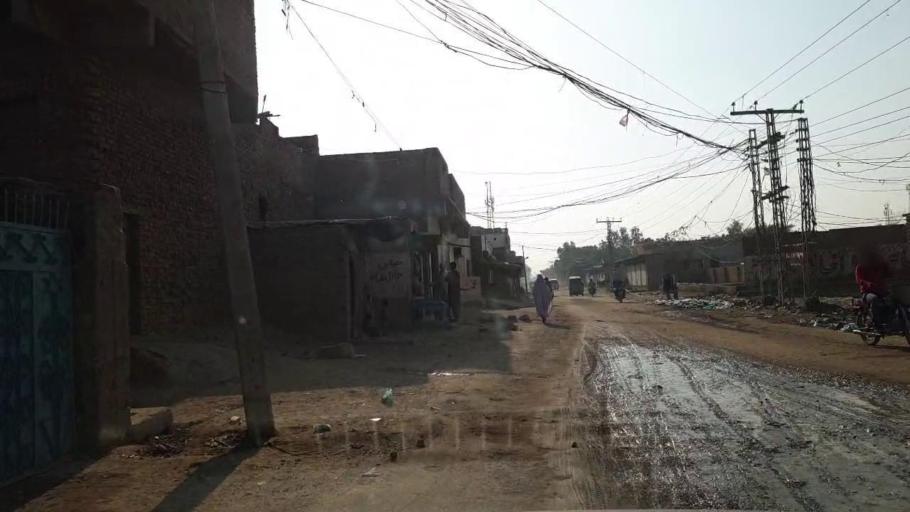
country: PK
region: Sindh
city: Kotri
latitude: 25.3559
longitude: 68.2679
